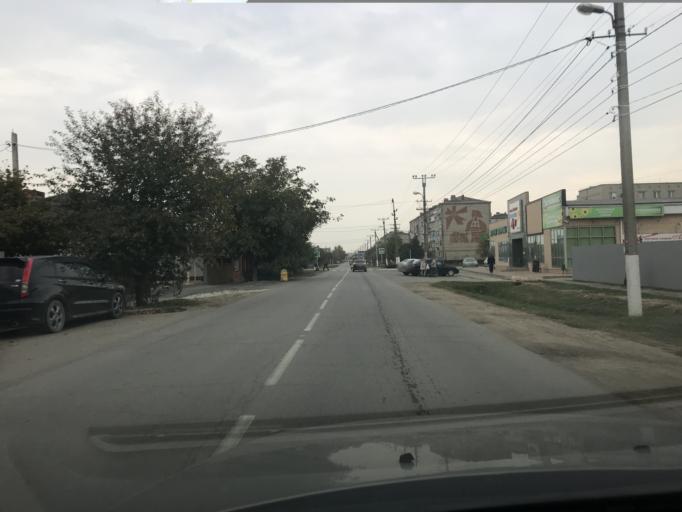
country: RU
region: Krasnodarskiy
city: Slavyansk-na-Kubani
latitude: 45.2674
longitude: 38.1073
